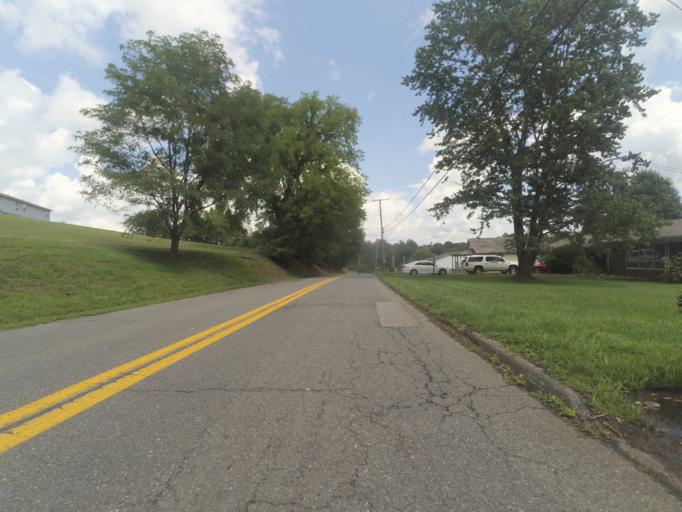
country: US
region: West Virginia
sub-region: Cabell County
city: Pea Ridge
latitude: 38.4059
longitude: -82.3775
